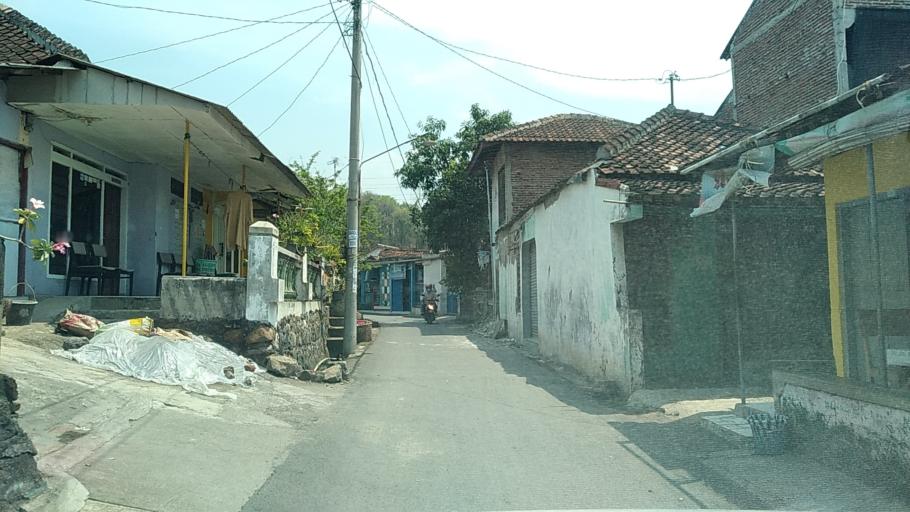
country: ID
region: Central Java
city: Semarang
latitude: -6.9745
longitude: 110.2983
